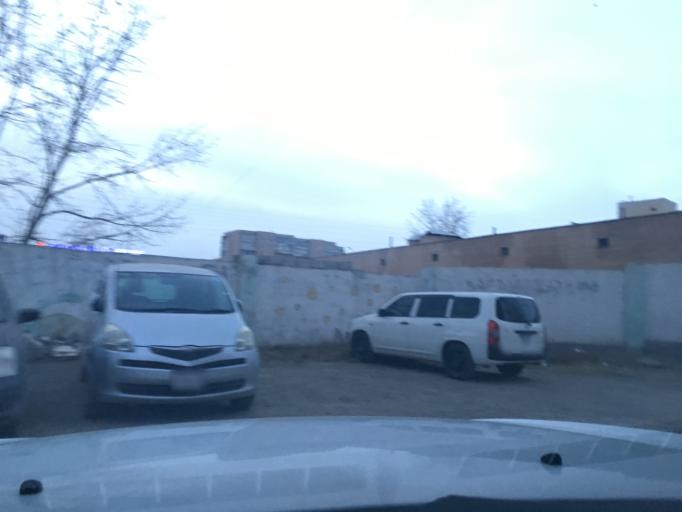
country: MN
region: Ulaanbaatar
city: Ulaanbaatar
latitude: 47.9156
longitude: 106.8564
